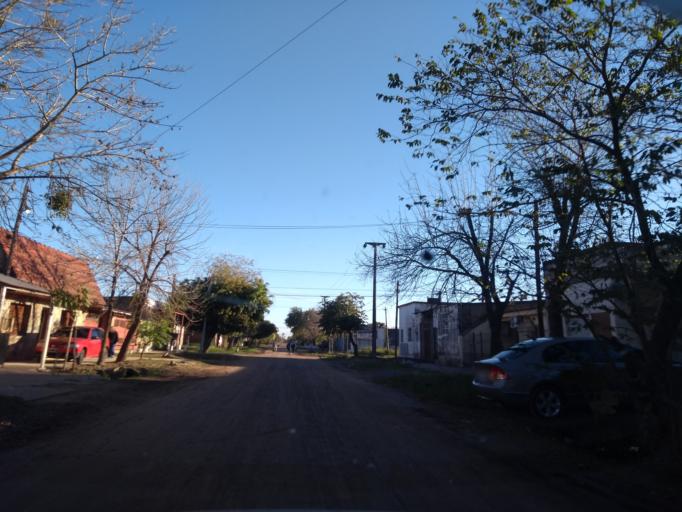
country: AR
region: Chaco
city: Barranqueras
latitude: -27.4880
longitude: -58.9331
